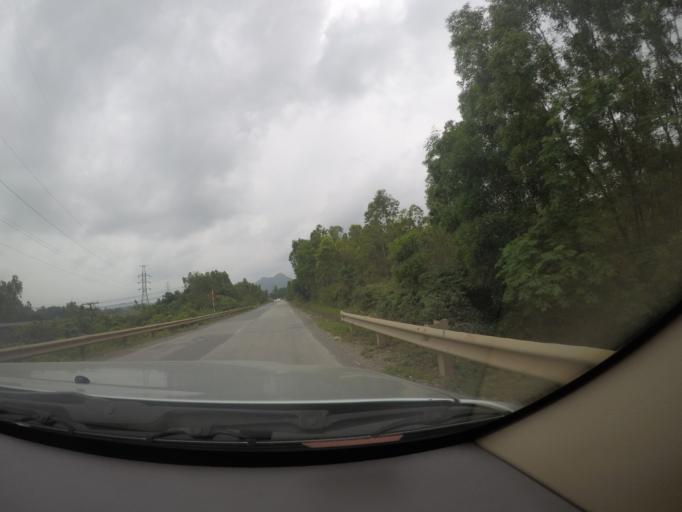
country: VN
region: Quang Binh
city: Quan Hau
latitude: 17.3308
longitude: 106.6247
